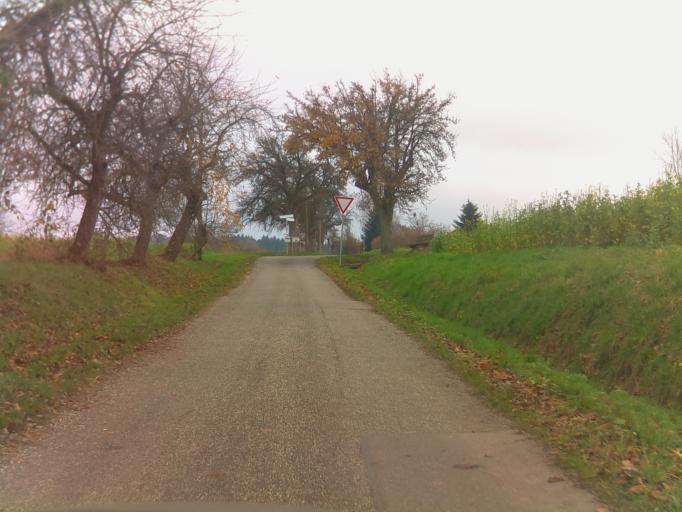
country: DE
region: Baden-Wuerttemberg
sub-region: Karlsruhe Region
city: Neunkirchen
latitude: 49.3930
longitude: 9.0187
